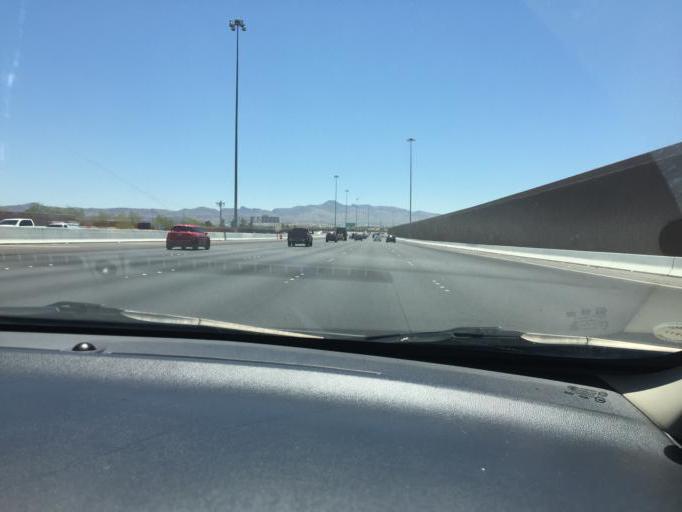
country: US
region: Nevada
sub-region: Clark County
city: Paradise
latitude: 36.0556
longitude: -115.1394
